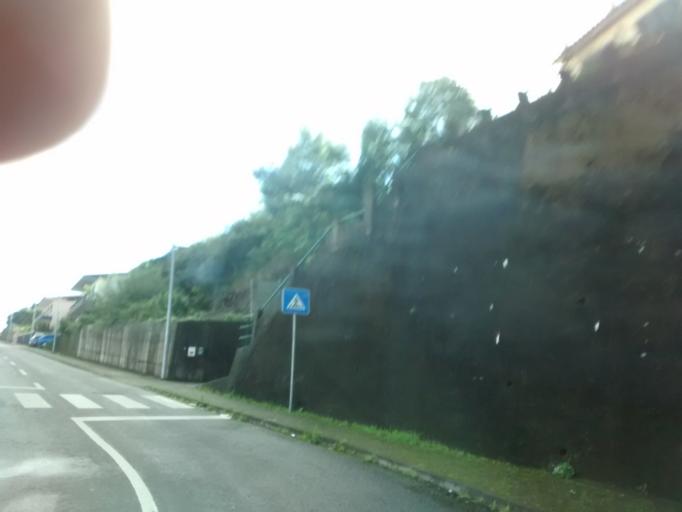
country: PT
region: Madeira
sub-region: Santana
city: Santana
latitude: 32.8050
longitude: -16.8850
